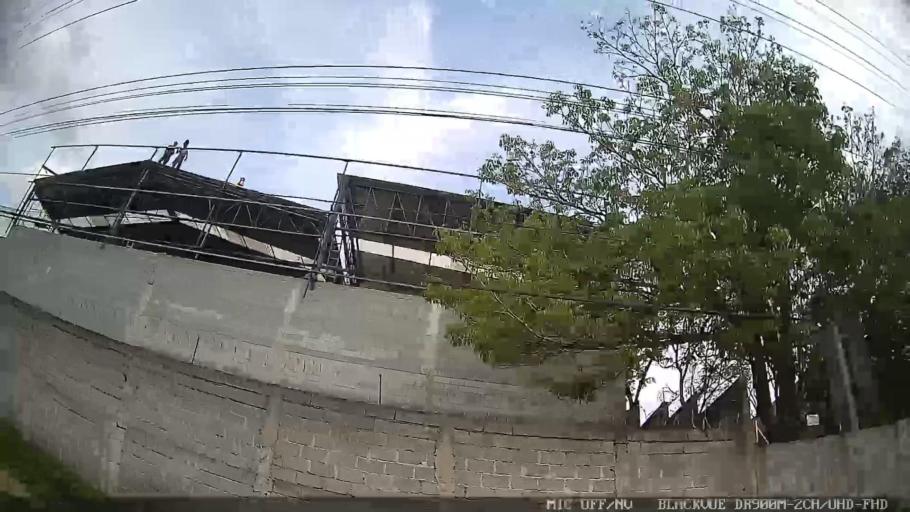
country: BR
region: Sao Paulo
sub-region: Braganca Paulista
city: Braganca Paulista
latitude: -22.9394
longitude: -46.5236
